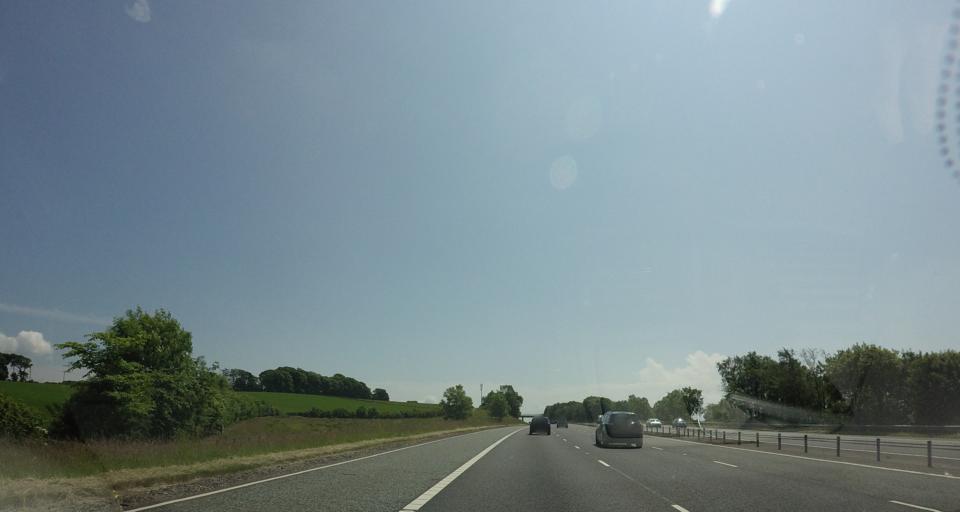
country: GB
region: Scotland
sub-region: Dumfries and Galloway
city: Annan
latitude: 55.0378
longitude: -3.1754
